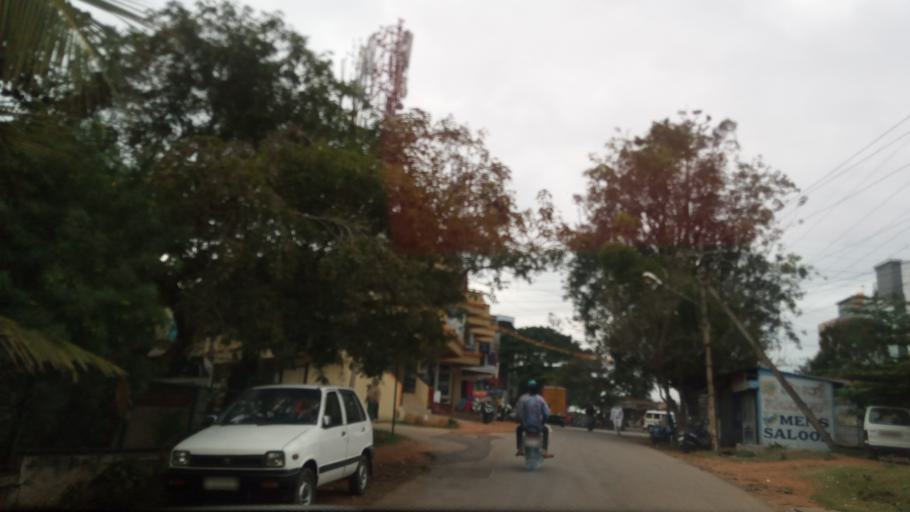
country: IN
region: Karnataka
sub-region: Mysore
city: Mysore
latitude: 12.2950
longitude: 76.6141
